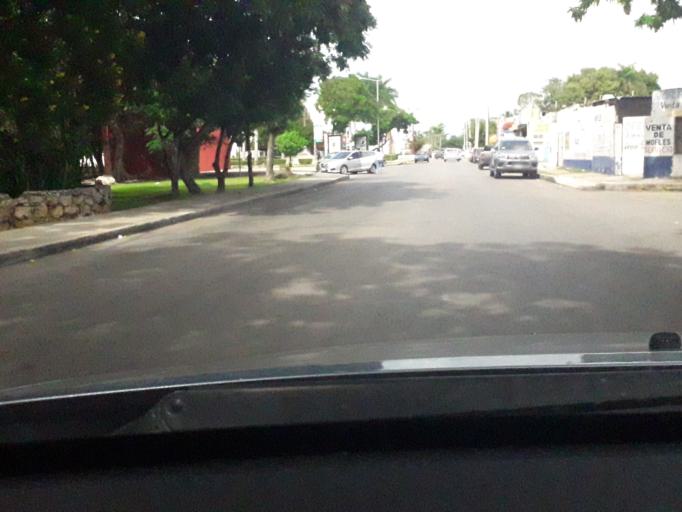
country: MX
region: Yucatan
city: Merida
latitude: 20.9758
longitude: -89.6556
